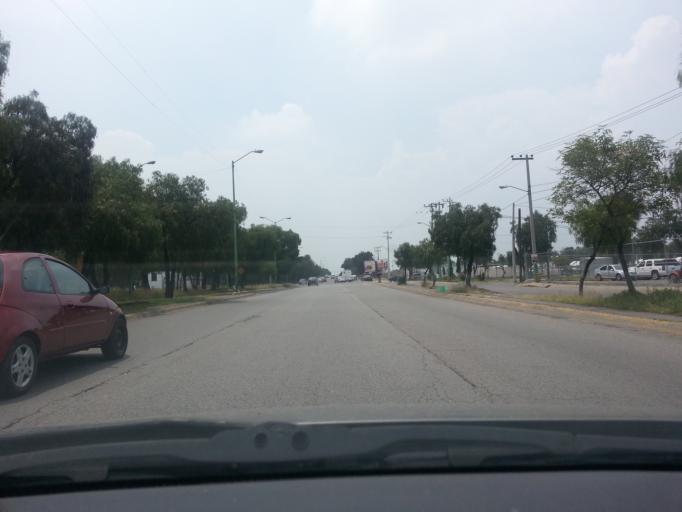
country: MX
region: Mexico
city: Cuautitlan Izcalli
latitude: 19.6580
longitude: -99.2034
